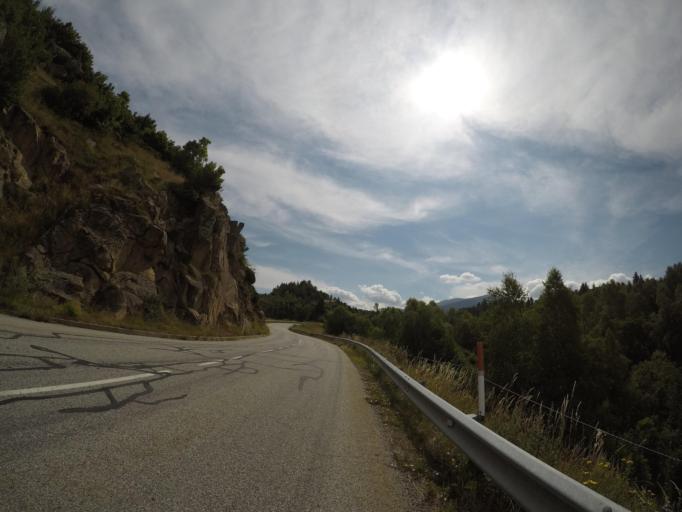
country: ES
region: Catalonia
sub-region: Provincia de Girona
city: Llivia
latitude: 42.4856
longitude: 2.0581
